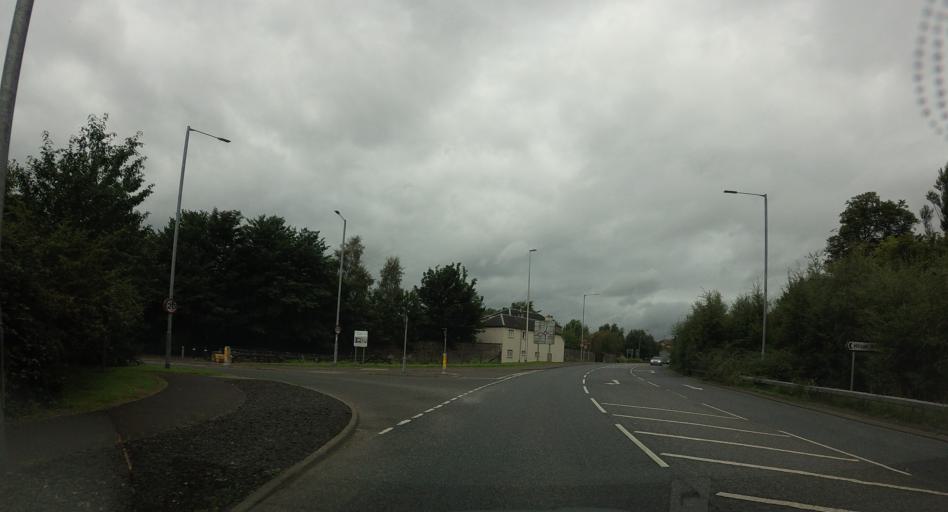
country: GB
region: Scotland
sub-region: Clackmannanshire
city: Alloa
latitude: 56.1200
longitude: -3.7786
